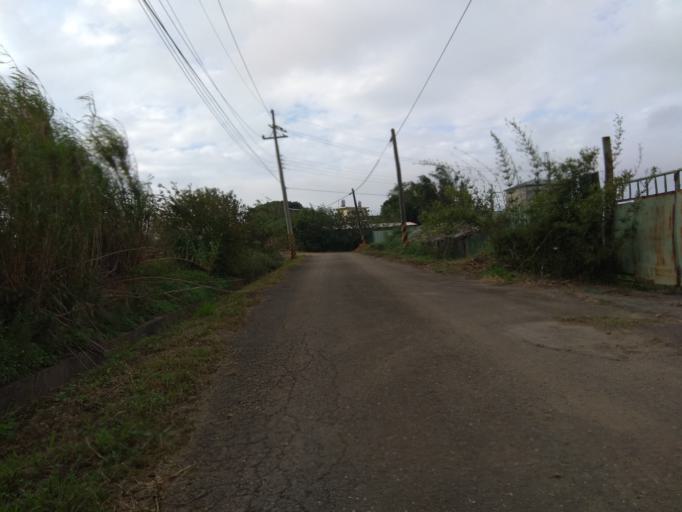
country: TW
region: Taiwan
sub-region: Hsinchu
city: Zhubei
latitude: 24.9712
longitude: 121.0434
